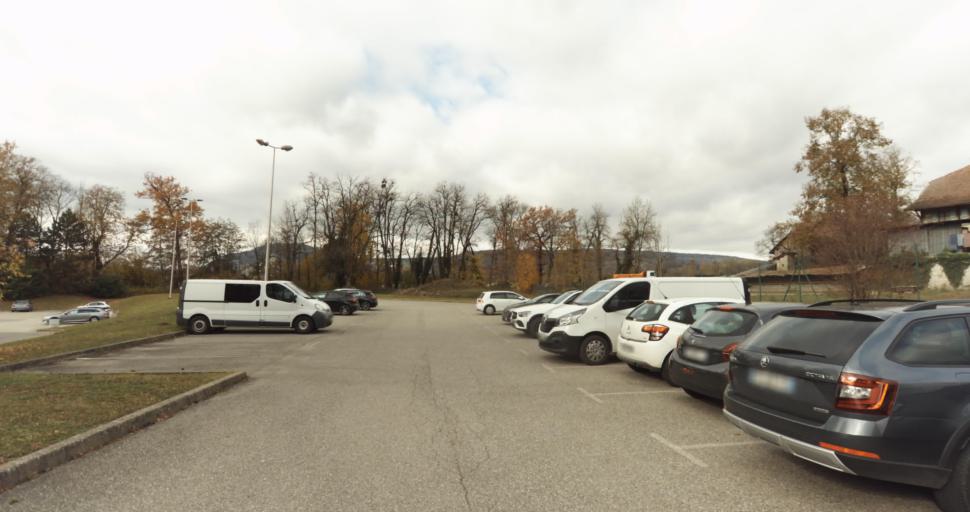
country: FR
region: Rhone-Alpes
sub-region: Departement de la Haute-Savoie
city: Pringy
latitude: 45.9391
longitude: 6.1189
